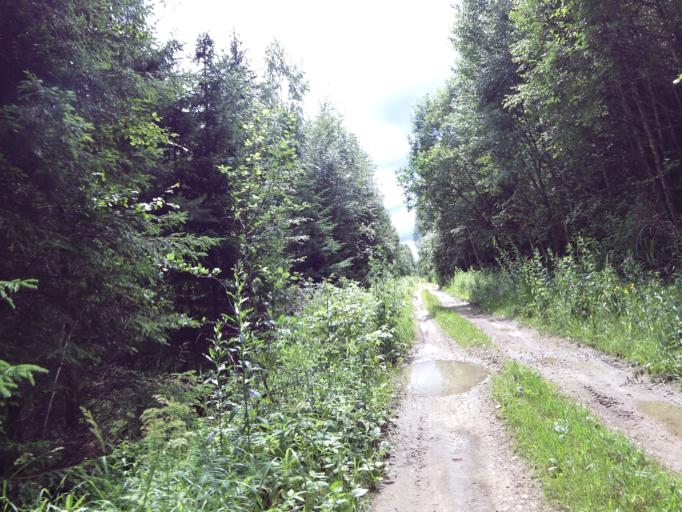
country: RU
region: Moskovskaya
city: Popovo
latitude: 54.9741
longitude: 37.6958
